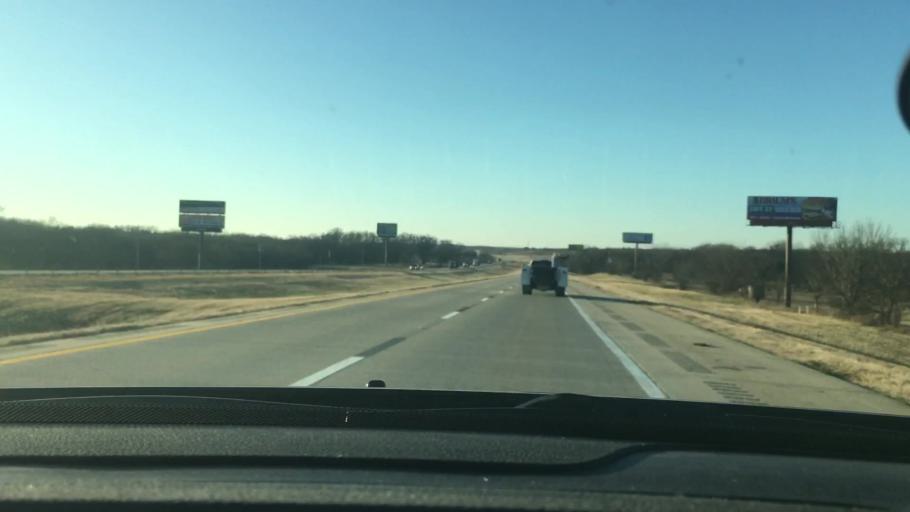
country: US
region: Oklahoma
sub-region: Carter County
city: Ardmore
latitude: 34.2721
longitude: -97.1626
